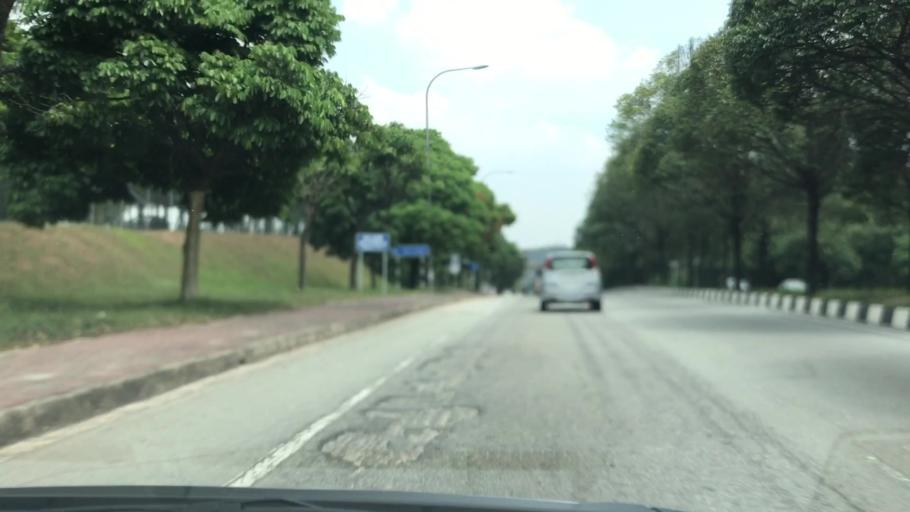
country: MY
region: Selangor
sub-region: Petaling
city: Petaling Jaya
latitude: 3.0557
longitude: 101.6616
